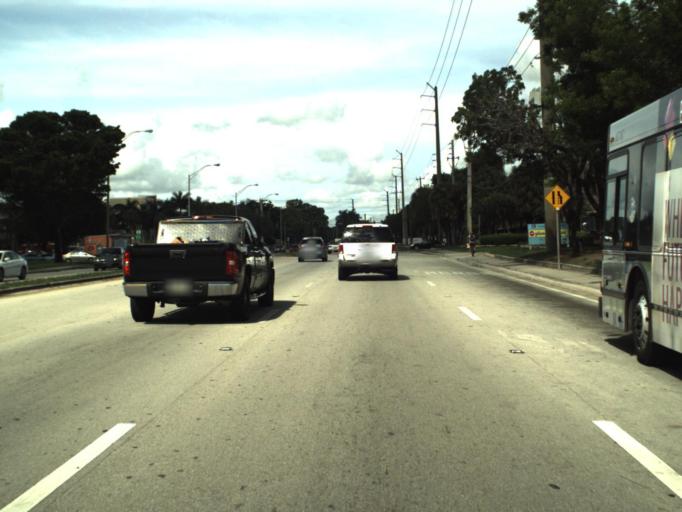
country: US
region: Florida
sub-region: Miami-Dade County
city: Country Club
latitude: 25.9425
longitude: -80.3080
